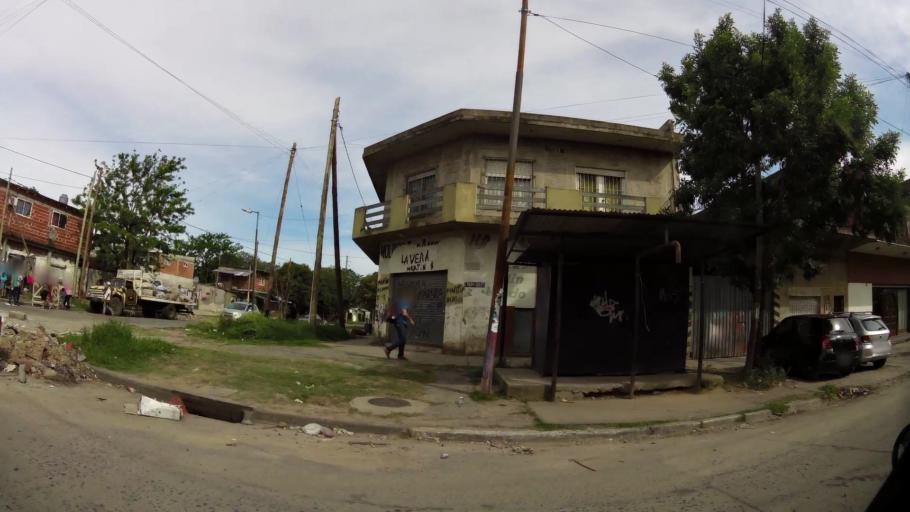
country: AR
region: Buenos Aires
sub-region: Partido de Quilmes
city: Quilmes
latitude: -34.7484
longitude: -58.2817
